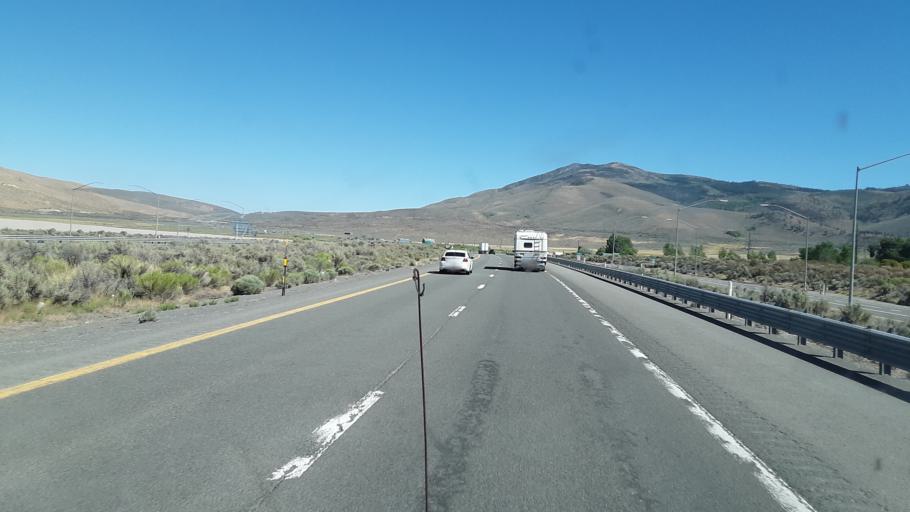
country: US
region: Nevada
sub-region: Washoe County
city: Cold Springs
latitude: 39.6555
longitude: -119.9860
